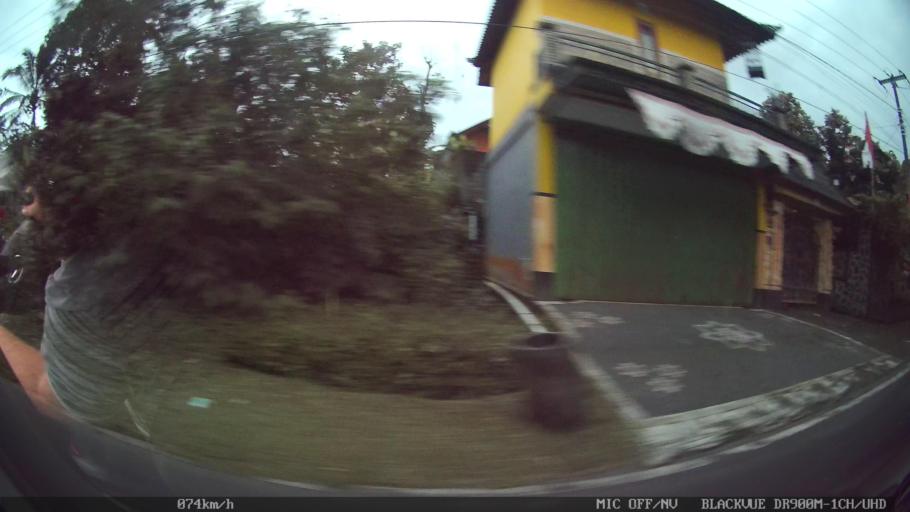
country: ID
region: Bali
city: Penebel
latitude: -8.4109
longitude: 115.1454
